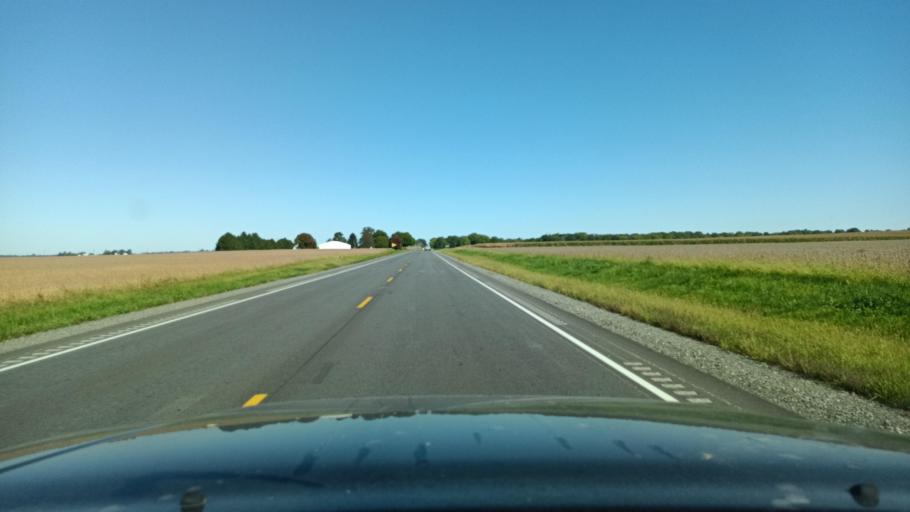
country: US
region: Illinois
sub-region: Champaign County
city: Philo
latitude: 39.9870
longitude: -88.1613
